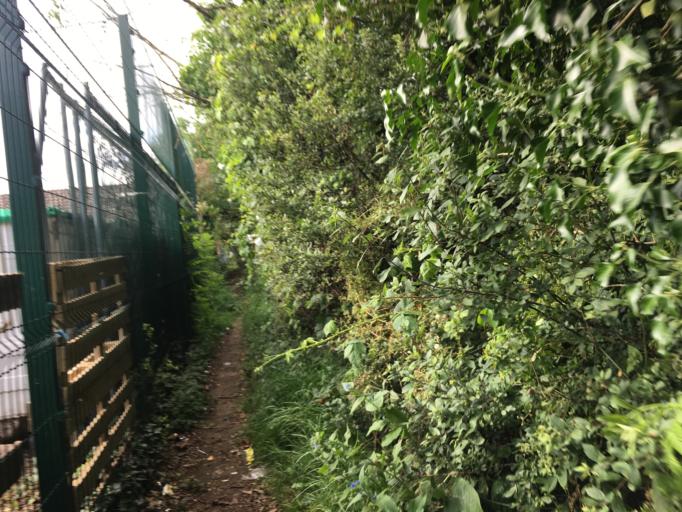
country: GB
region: England
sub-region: Warwickshire
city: Rugby
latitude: 52.3573
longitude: -1.2298
